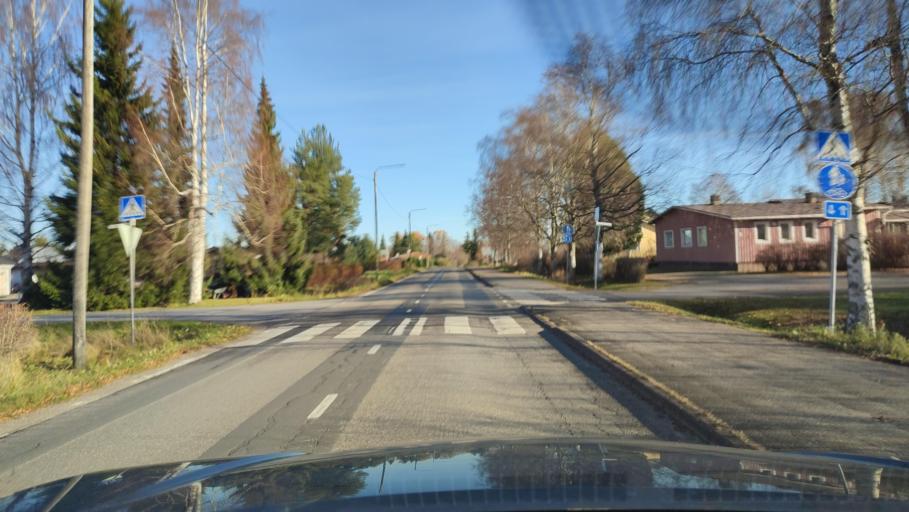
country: FI
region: Southern Ostrobothnia
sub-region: Suupohja
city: Teuva
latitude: 62.4877
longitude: 21.7533
